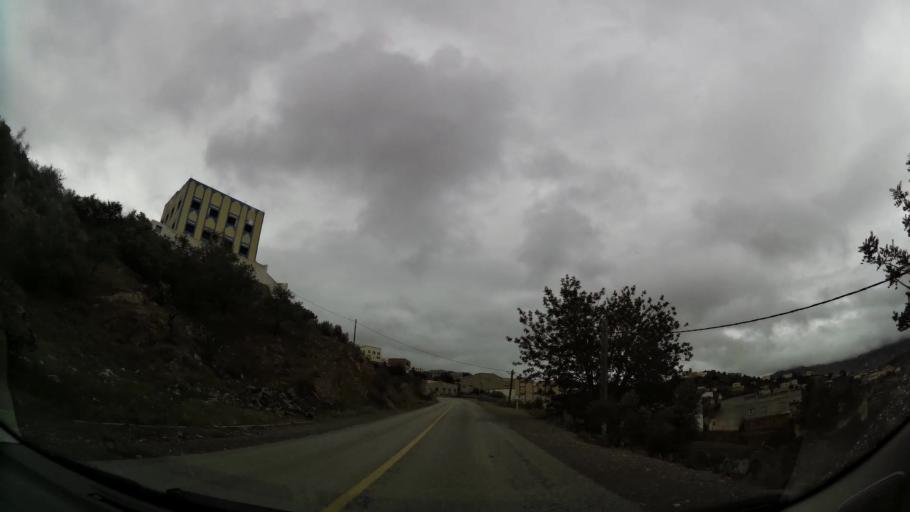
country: MA
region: Taza-Al Hoceima-Taounate
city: Imzourene
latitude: 34.9564
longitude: -3.8100
